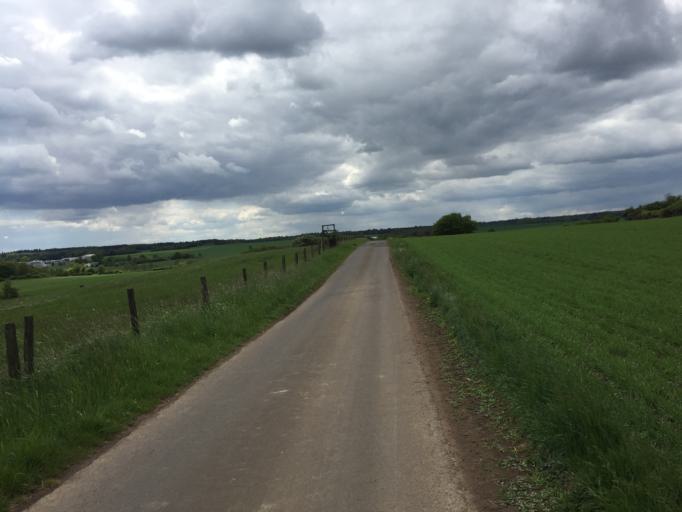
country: DE
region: Hesse
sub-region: Regierungsbezirk Giessen
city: Grunberg
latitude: 50.5733
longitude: 8.9009
